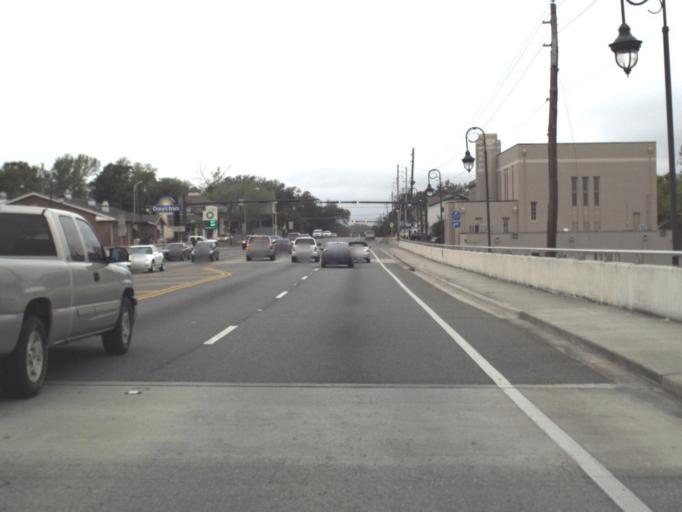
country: US
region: Florida
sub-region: Escambia County
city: Pensacola
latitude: 30.4216
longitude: -87.2159
